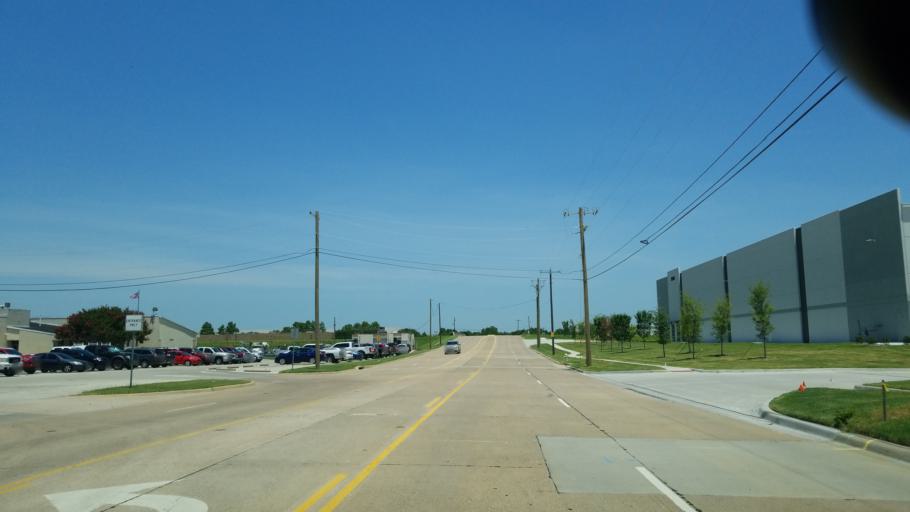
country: US
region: Texas
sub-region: Dallas County
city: Farmers Branch
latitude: 32.9246
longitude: -96.9096
